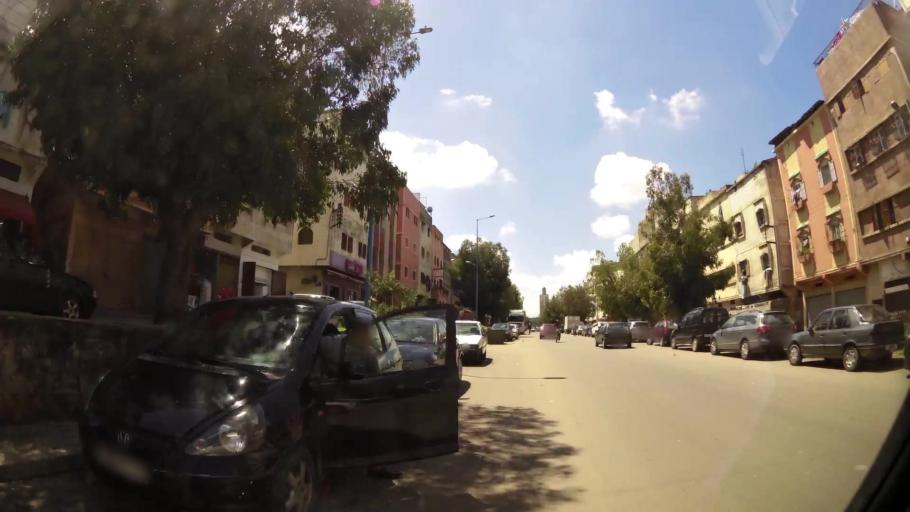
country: MA
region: Grand Casablanca
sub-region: Casablanca
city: Casablanca
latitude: 33.5622
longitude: -7.5674
